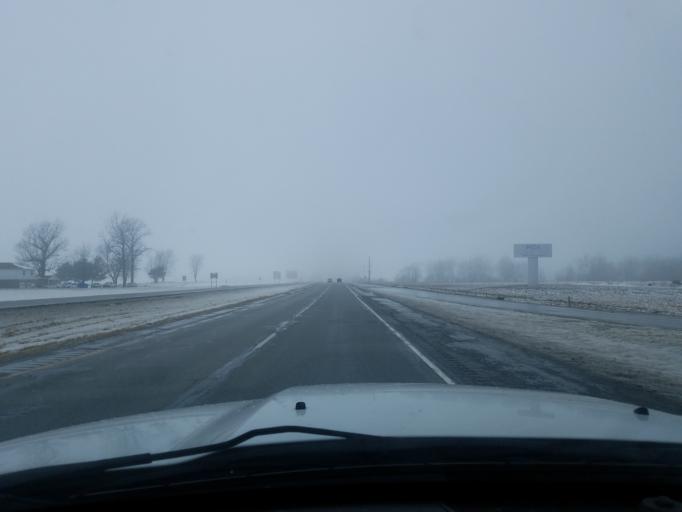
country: US
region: Indiana
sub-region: Tipton County
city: Tipton
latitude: 40.2775
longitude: -86.1271
